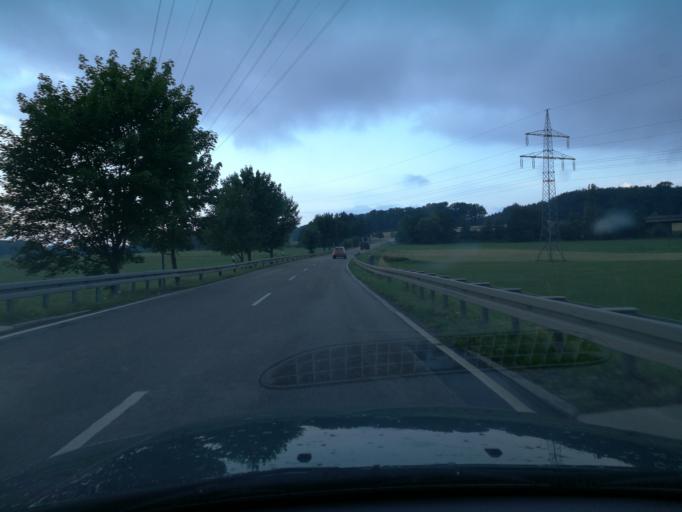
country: DE
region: Bavaria
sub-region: Regierungsbezirk Mittelfranken
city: Obermichelbach
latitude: 49.5612
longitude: 10.9507
